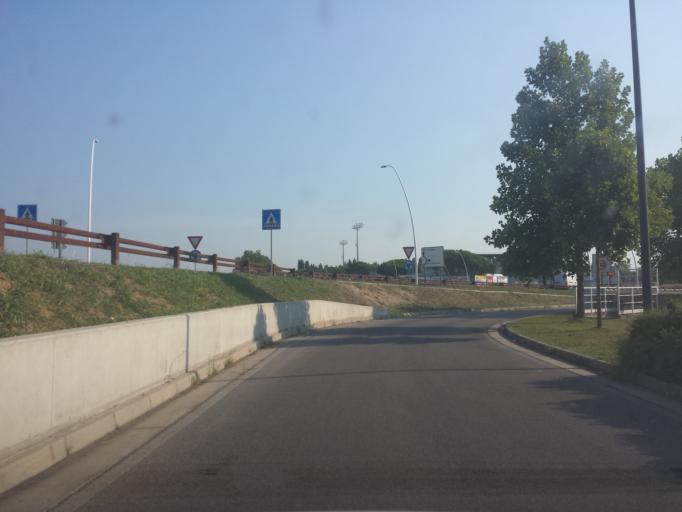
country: IT
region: Veneto
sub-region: Provincia di Venezia
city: Lido di Iesolo
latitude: 45.5087
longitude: 12.6353
